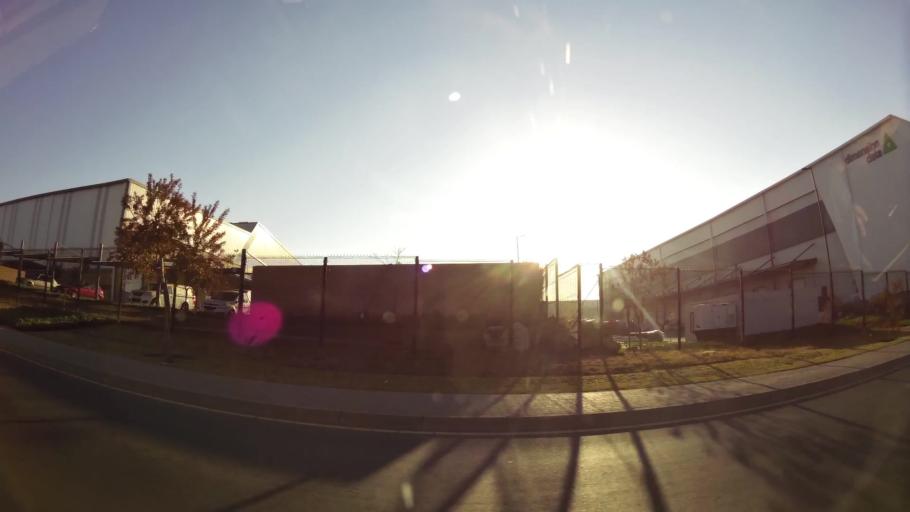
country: ZA
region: Gauteng
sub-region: City of Johannesburg Metropolitan Municipality
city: Midrand
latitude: -26.0247
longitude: 28.1198
